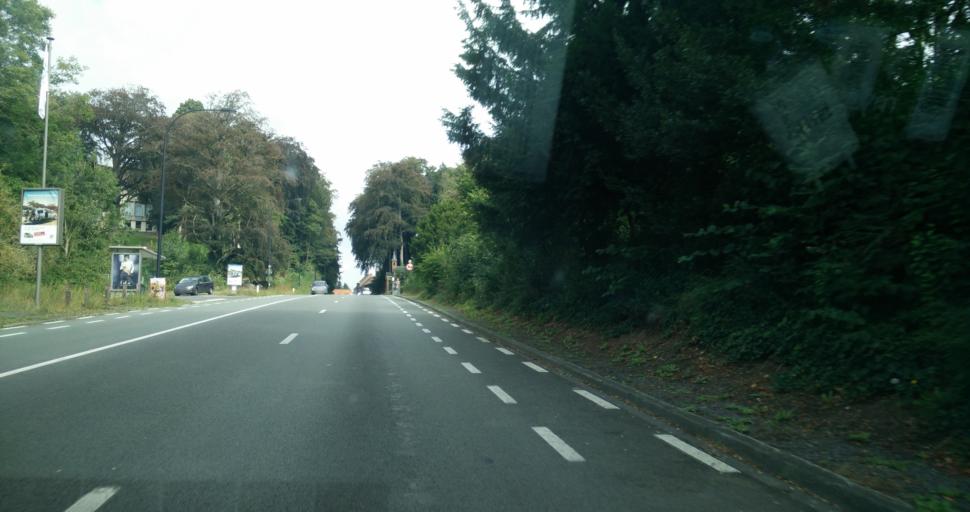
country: BE
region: Flanders
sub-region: Provincie Oost-Vlaanderen
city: Ronse
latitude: 50.7591
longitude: 3.5873
